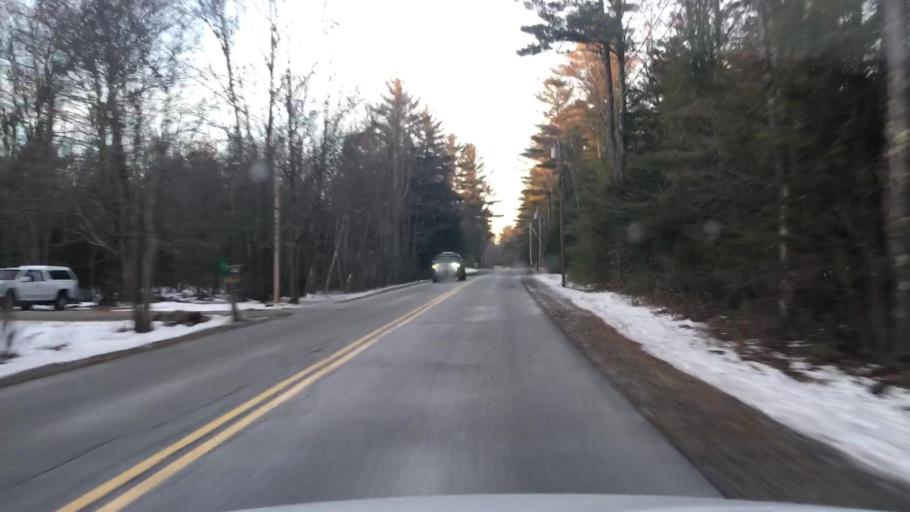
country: US
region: Maine
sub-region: York County
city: Berwick
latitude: 43.3286
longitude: -70.8646
